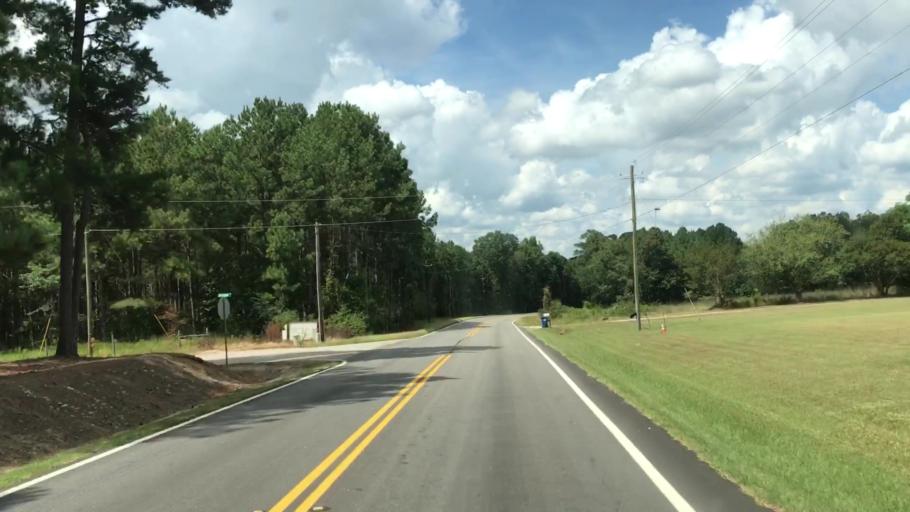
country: US
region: Georgia
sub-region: Greene County
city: Greensboro
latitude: 33.5594
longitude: -83.1348
